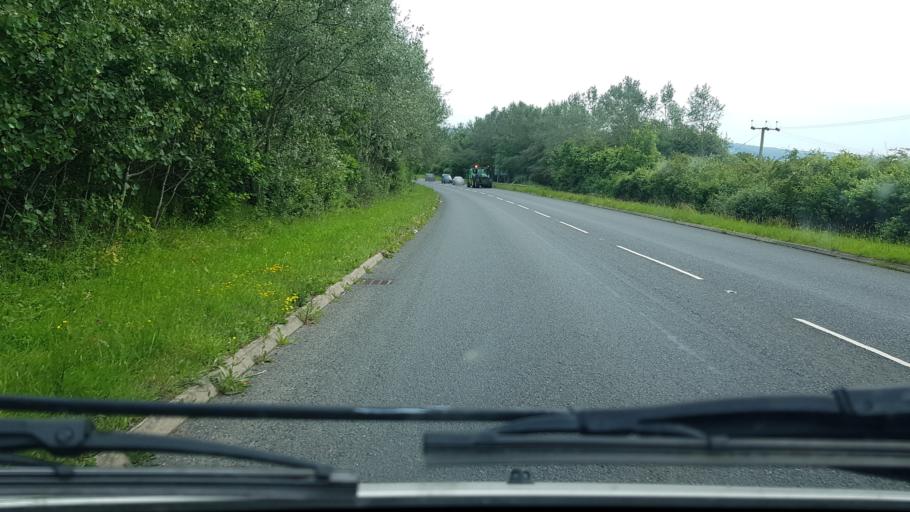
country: GB
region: England
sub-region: Worcestershire
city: Broadway
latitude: 52.0493
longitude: -1.8753
